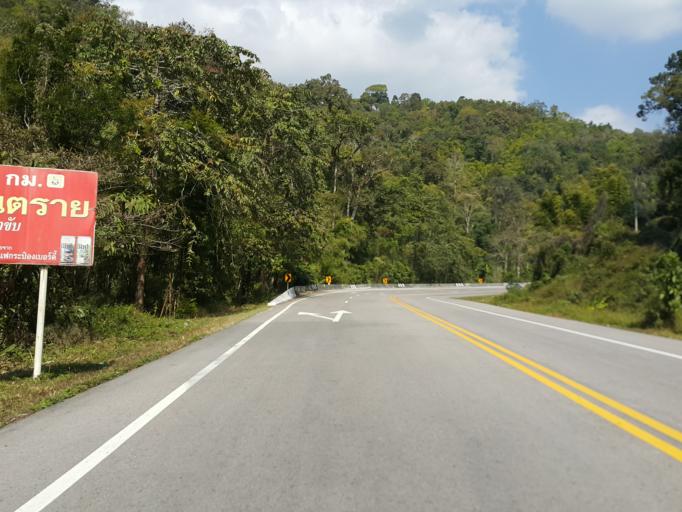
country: TH
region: Lampang
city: Wang Nuea
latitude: 19.0547
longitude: 99.3545
